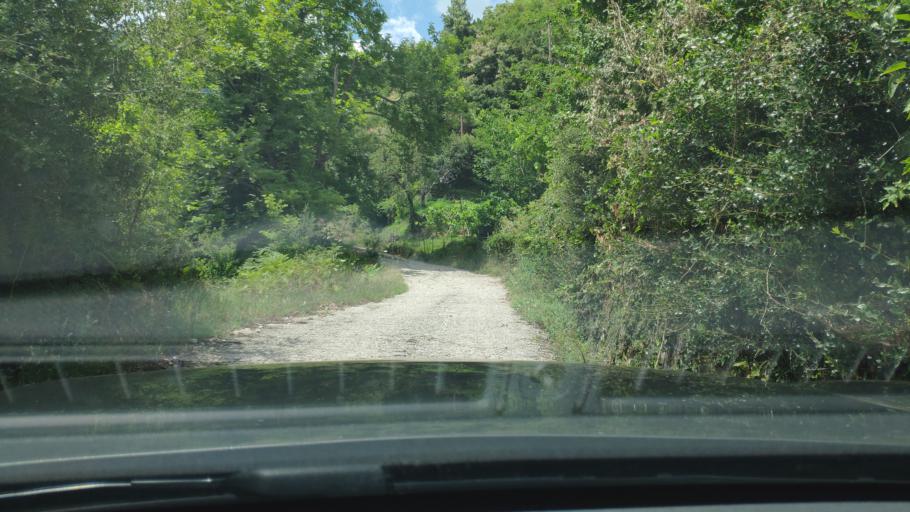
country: GR
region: Epirus
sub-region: Nomos Artas
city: Agios Dimitrios
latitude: 39.3210
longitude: 21.0042
